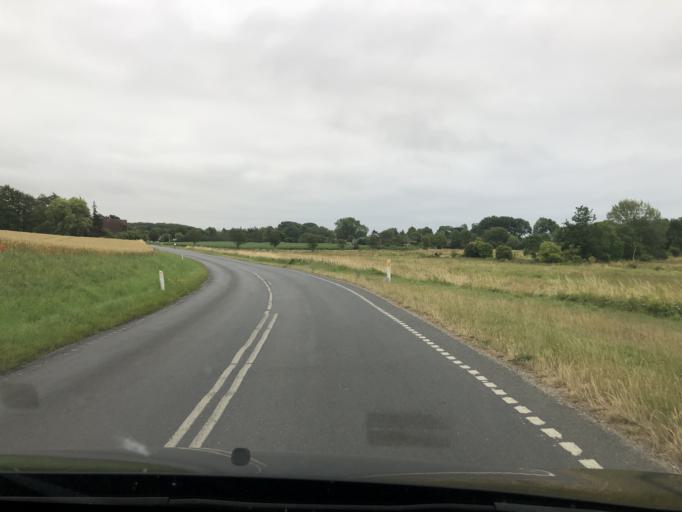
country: DK
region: South Denmark
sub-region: AEro Kommune
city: AEroskobing
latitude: 54.9165
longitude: 10.2807
